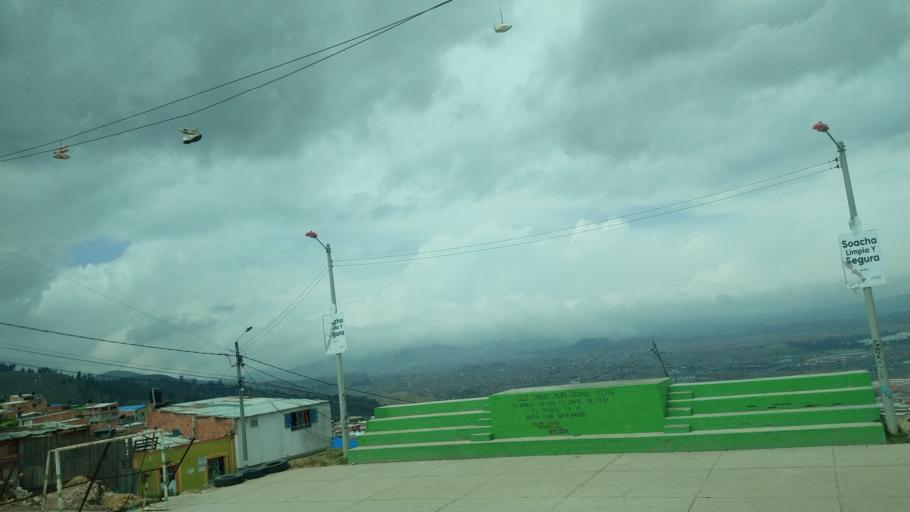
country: CO
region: Cundinamarca
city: Soacha
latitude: 4.5793
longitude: -74.1831
